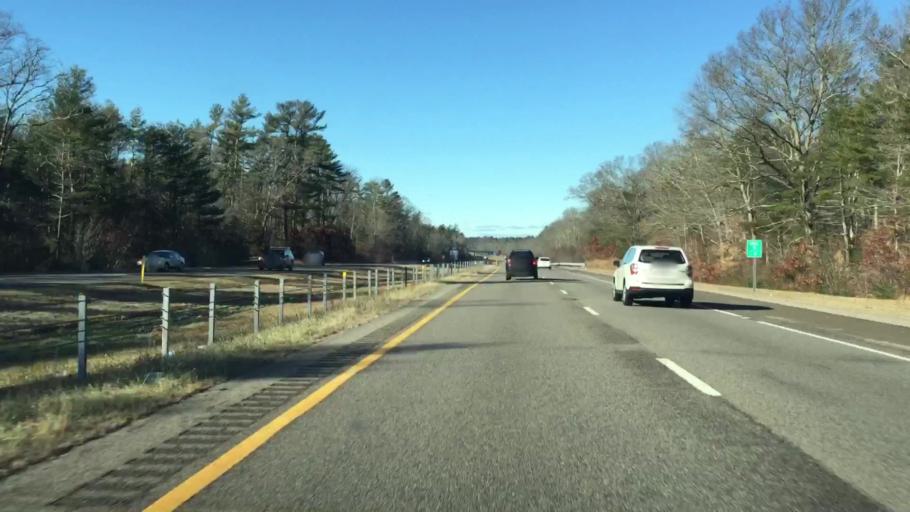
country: US
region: Massachusetts
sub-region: Plymouth County
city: Middleborough Center
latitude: 41.8609
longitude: -70.8785
